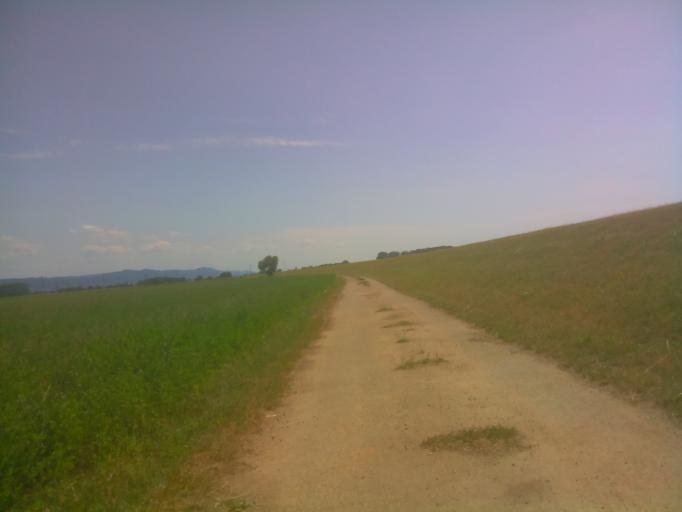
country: DE
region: Hesse
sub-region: Regierungsbezirk Darmstadt
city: Heppenheim an der Bergstrasse
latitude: 49.6095
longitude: 8.5987
